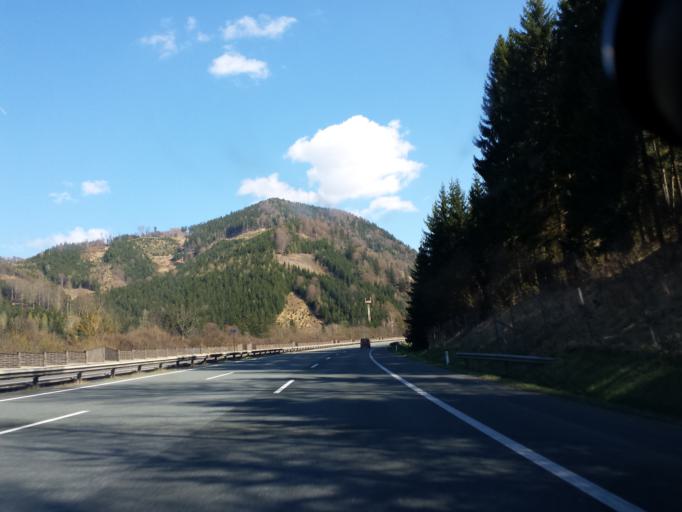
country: AT
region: Styria
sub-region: Politischer Bezirk Leoben
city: Sankt Michael in Obersteiermark
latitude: 47.3173
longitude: 15.0491
